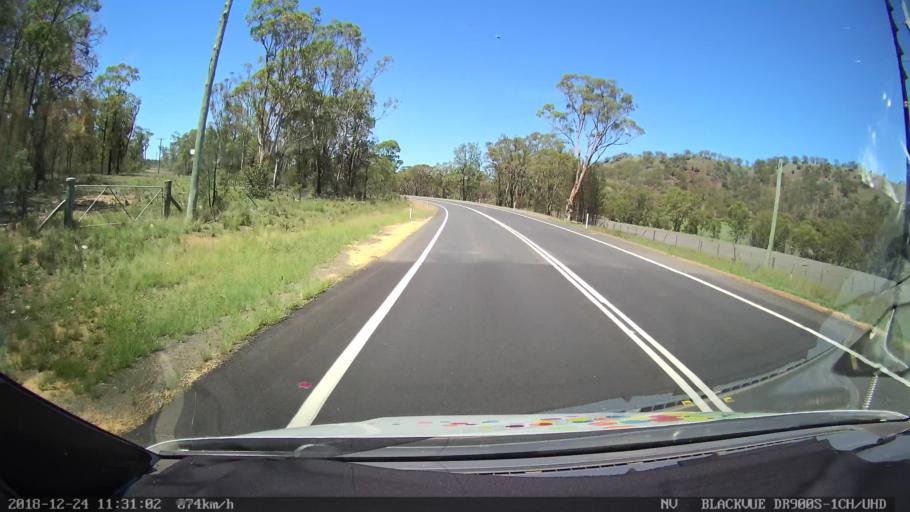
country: AU
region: New South Wales
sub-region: Upper Hunter Shire
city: Merriwa
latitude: -32.2110
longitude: 150.4617
